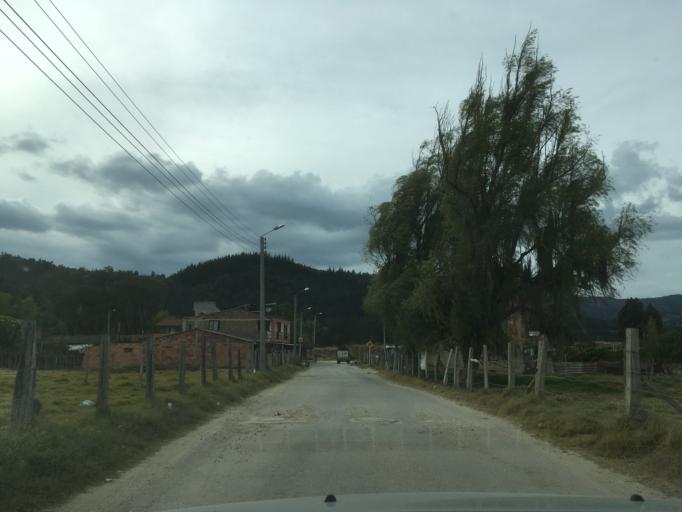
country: CO
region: Boyaca
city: Firavitoba
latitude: 5.6684
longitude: -72.9955
